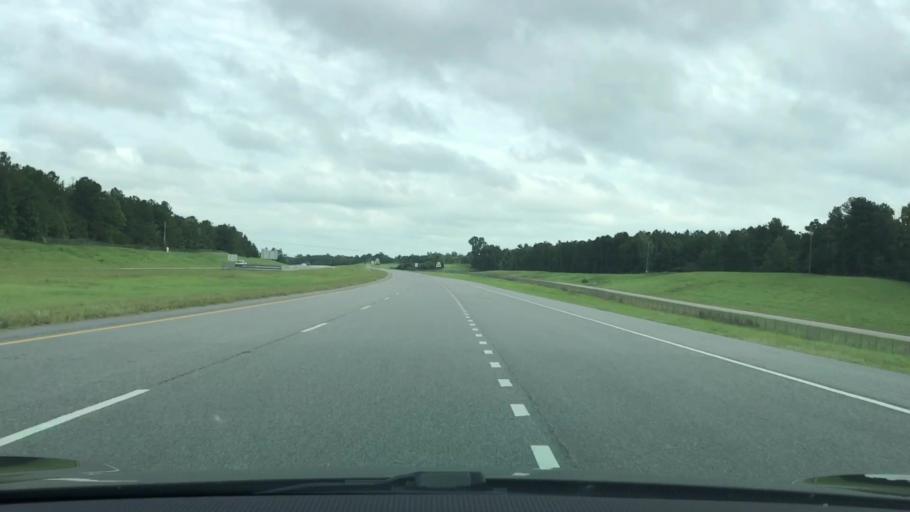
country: US
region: Alabama
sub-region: Montgomery County
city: Pike Road
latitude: 32.3423
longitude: -86.0636
